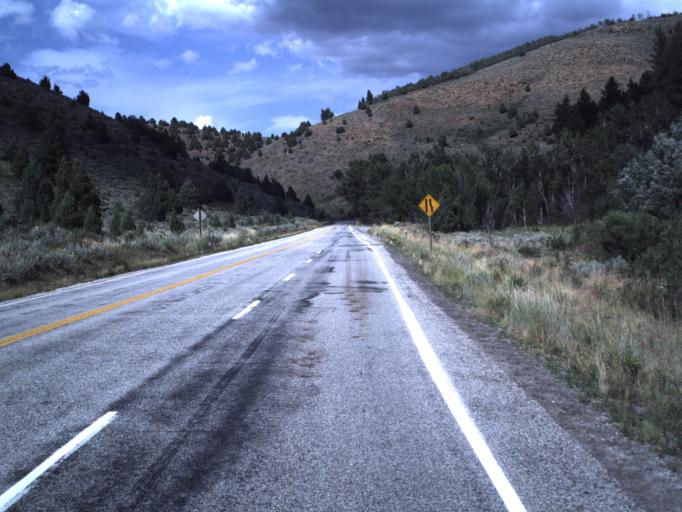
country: US
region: Utah
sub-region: Cache County
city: North Logan
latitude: 41.8454
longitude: -111.5881
